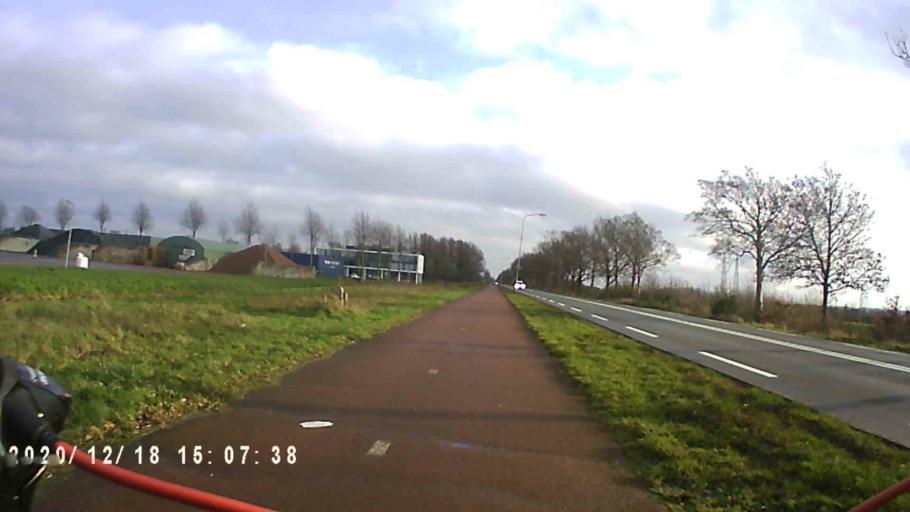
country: NL
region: Groningen
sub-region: Gemeente Hoogezand-Sappemeer
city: Hoogezand
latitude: 53.1714
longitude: 6.6905
